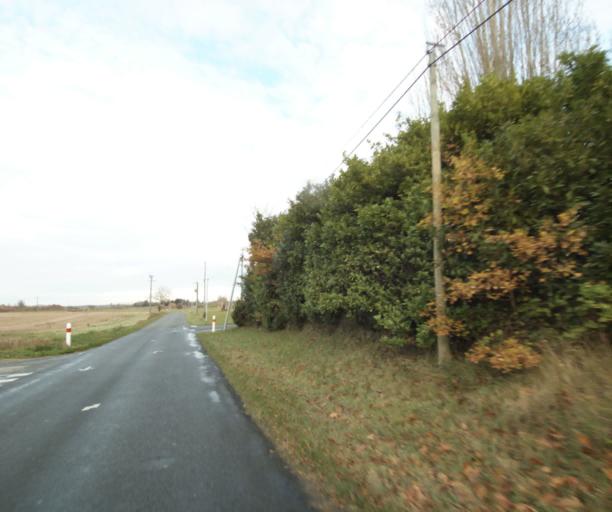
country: FR
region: Poitou-Charentes
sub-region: Departement de la Charente-Maritime
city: Corme-Royal
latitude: 45.7528
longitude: -0.8043
